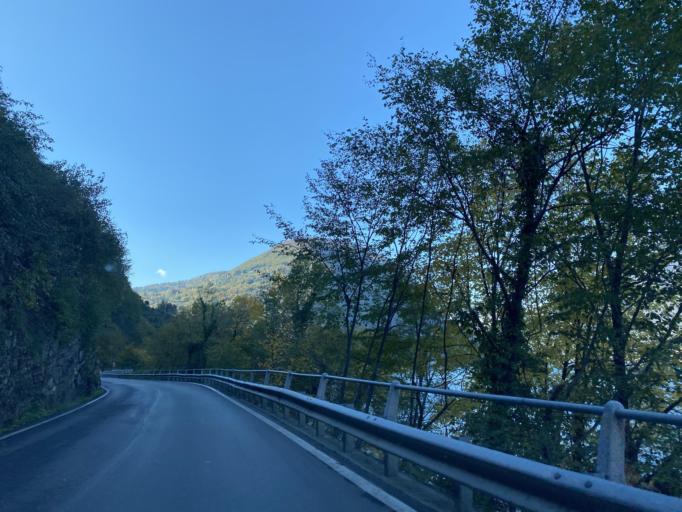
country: IT
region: Lombardy
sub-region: Provincia di Como
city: Osteno-Claino
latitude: 46.0106
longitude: 9.0993
